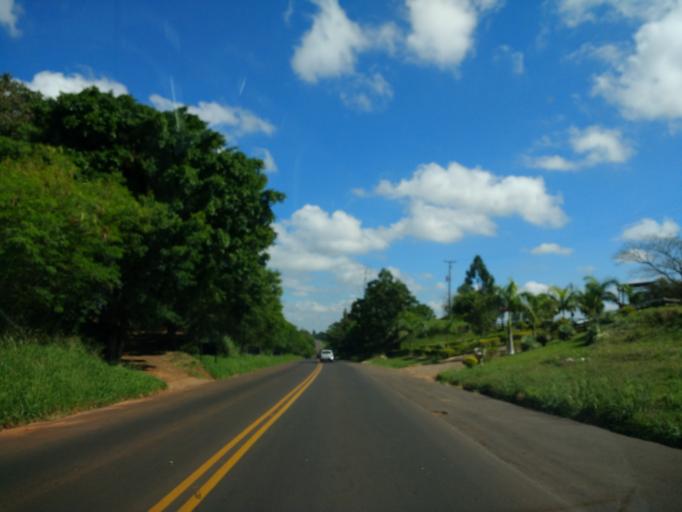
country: BR
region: Parana
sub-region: Umuarama
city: Umuarama
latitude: -23.8164
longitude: -53.3312
